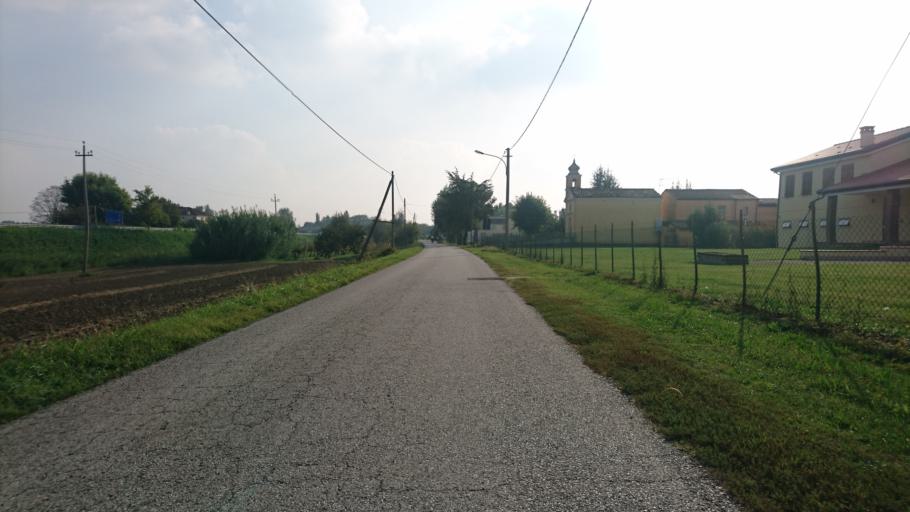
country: IT
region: Veneto
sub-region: Provincia di Rovigo
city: Polesella
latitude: 44.9737
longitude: 11.7546
